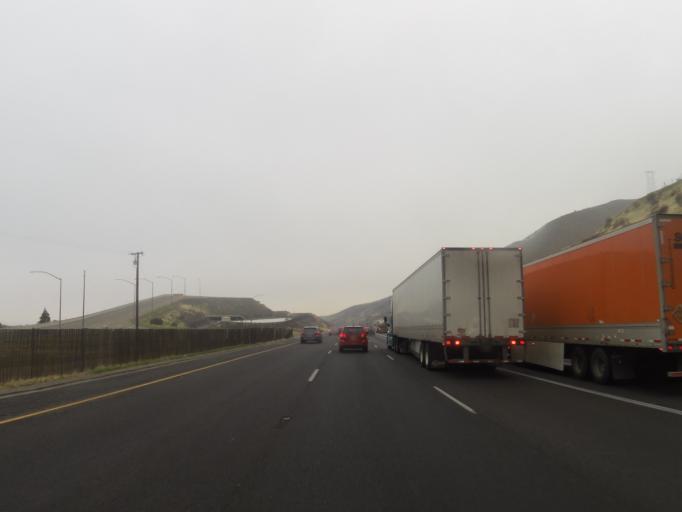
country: US
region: California
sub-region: Kern County
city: Lebec
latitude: 34.9208
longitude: -118.9236
